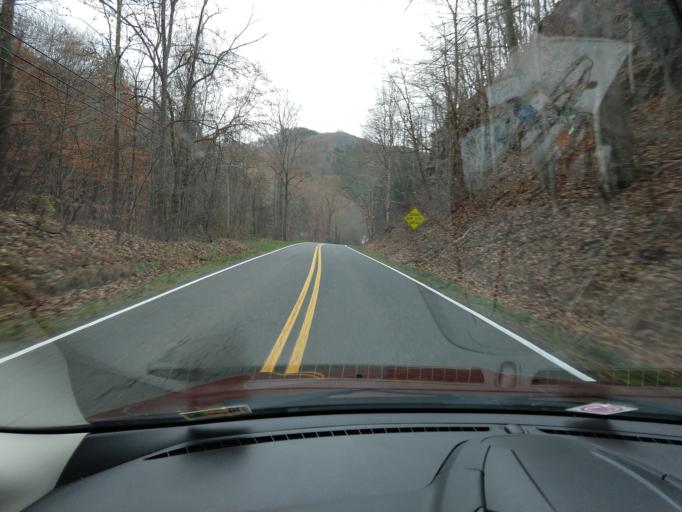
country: US
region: West Virginia
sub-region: Greenbrier County
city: White Sulphur Springs
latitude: 37.7322
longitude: -80.2273
